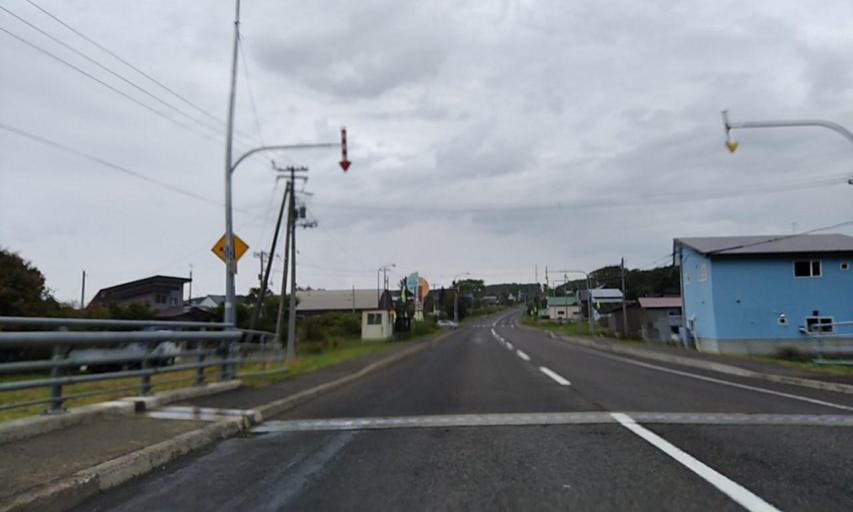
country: JP
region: Hokkaido
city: Mombetsu
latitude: 44.5283
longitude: 143.0437
